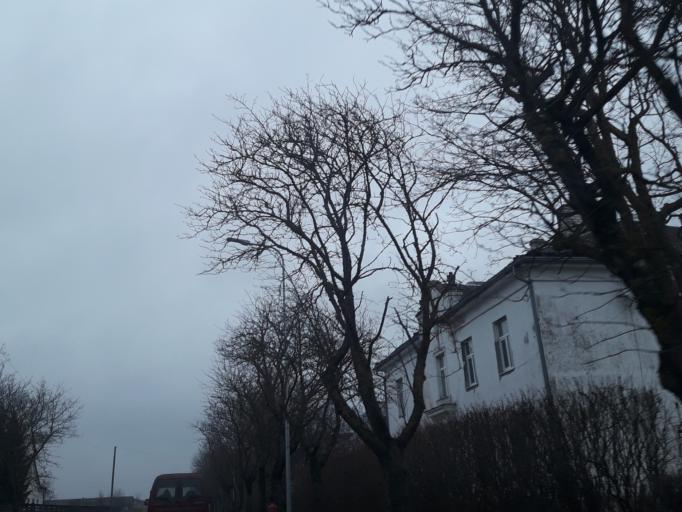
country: EE
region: Saare
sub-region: Kuressaare linn
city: Kuressaare
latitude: 58.2544
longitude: 22.4772
